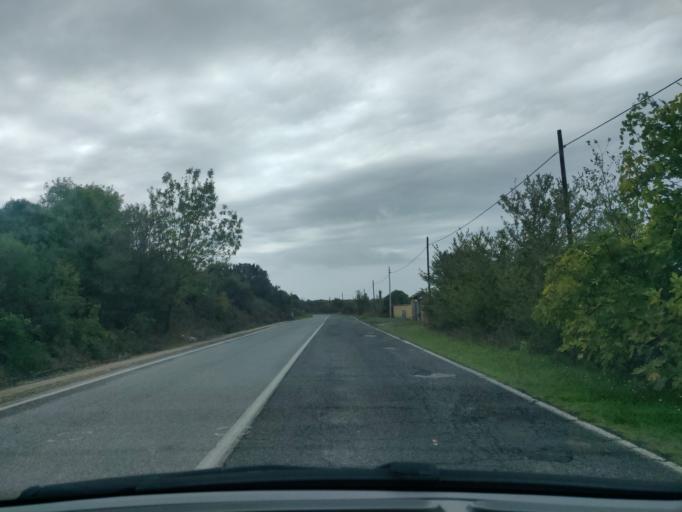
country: IT
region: Latium
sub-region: Citta metropolitana di Roma Capitale
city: Allumiere
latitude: 42.1209
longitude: 11.8626
